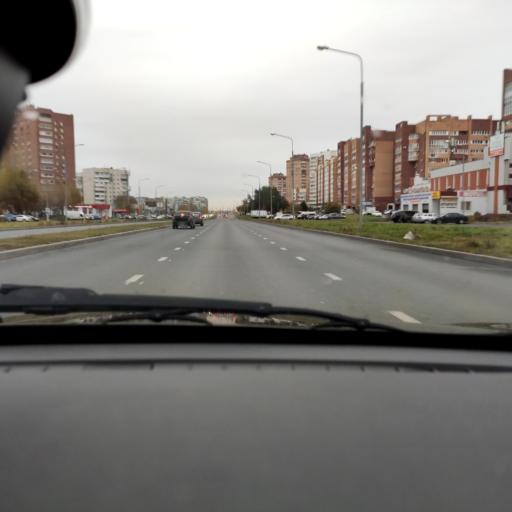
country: RU
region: Samara
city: Tol'yatti
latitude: 53.5365
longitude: 49.3535
